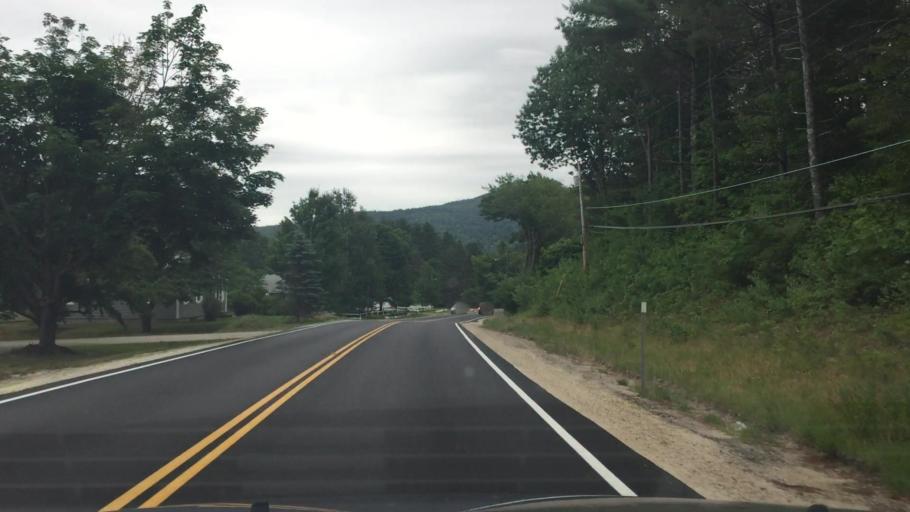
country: US
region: New Hampshire
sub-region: Carroll County
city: Freedom
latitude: 43.8045
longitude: -71.0605
